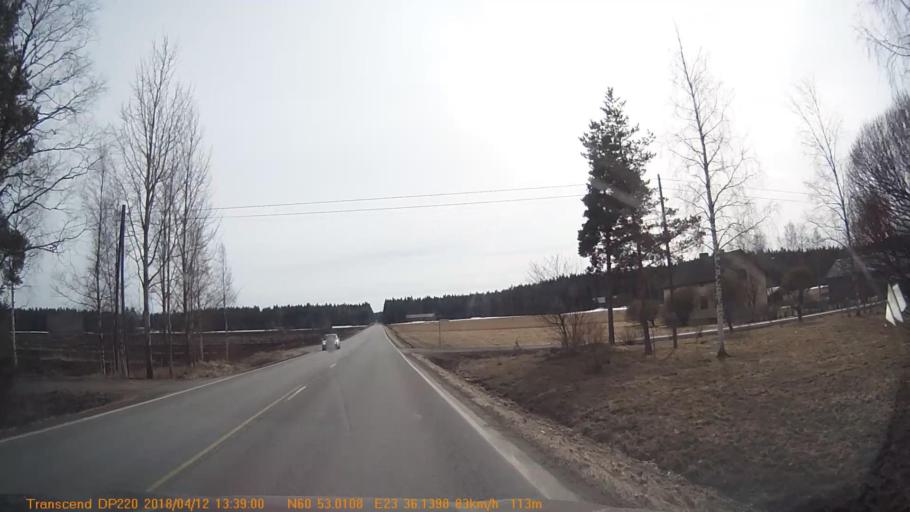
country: FI
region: Haeme
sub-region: Forssa
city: Forssa
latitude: 60.8832
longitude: 23.6024
